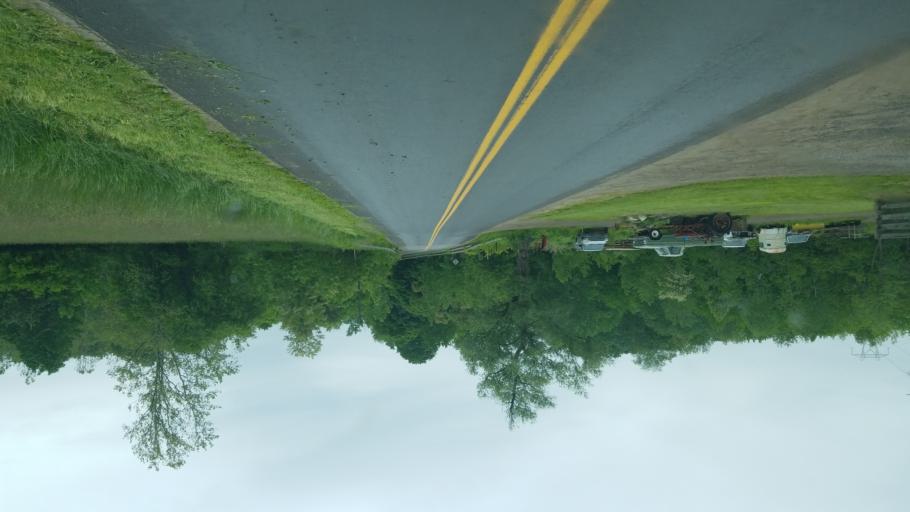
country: US
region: New York
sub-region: Herkimer County
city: Frankfort
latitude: 43.0917
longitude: -75.0874
